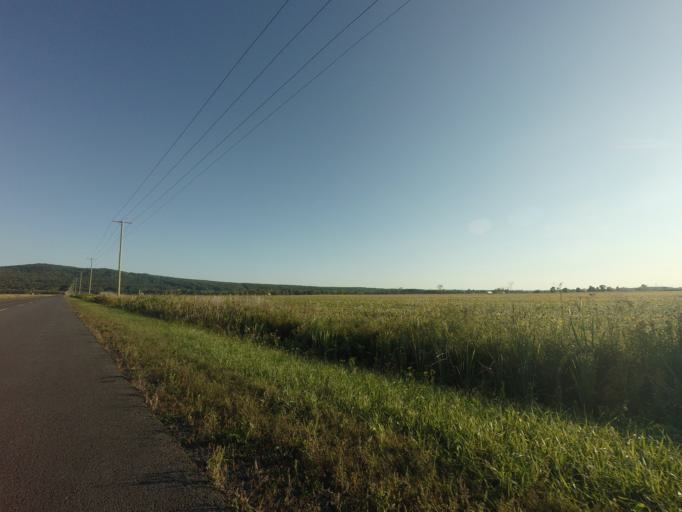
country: CA
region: Quebec
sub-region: Monteregie
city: Rigaud
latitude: 45.4816
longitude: -74.3460
